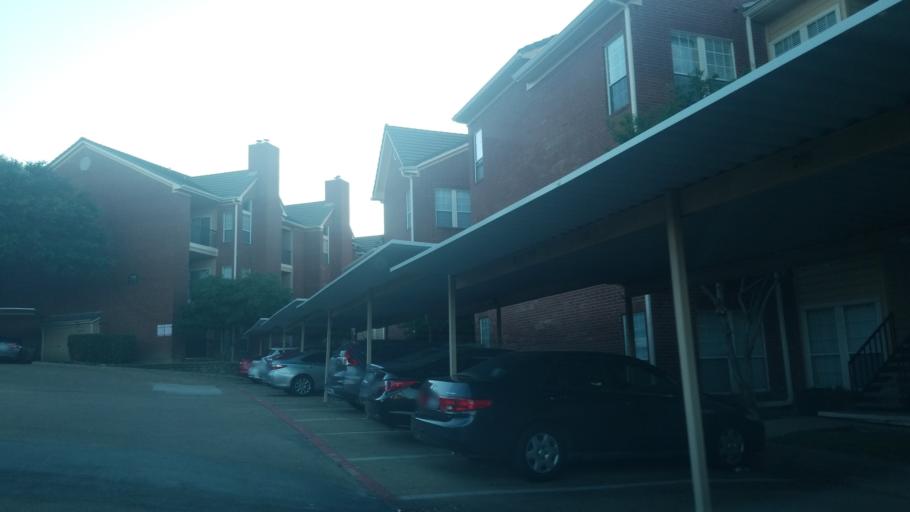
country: US
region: Texas
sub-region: Dallas County
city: Irving
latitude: 32.8787
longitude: -96.9645
